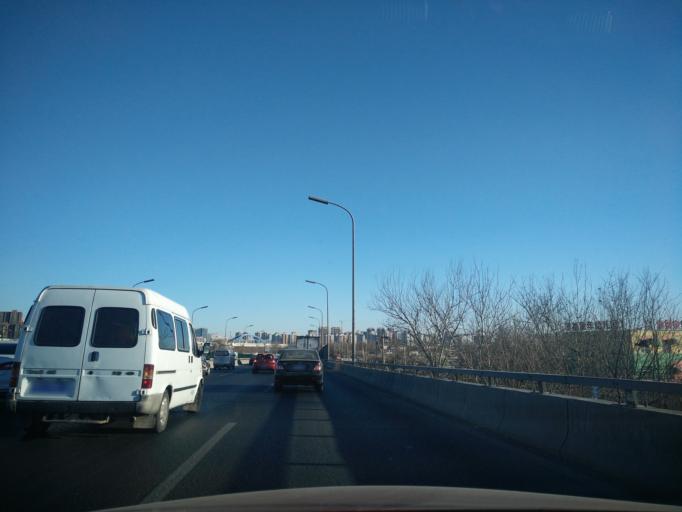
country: CN
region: Beijing
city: Lugu
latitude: 39.8829
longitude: 116.2031
